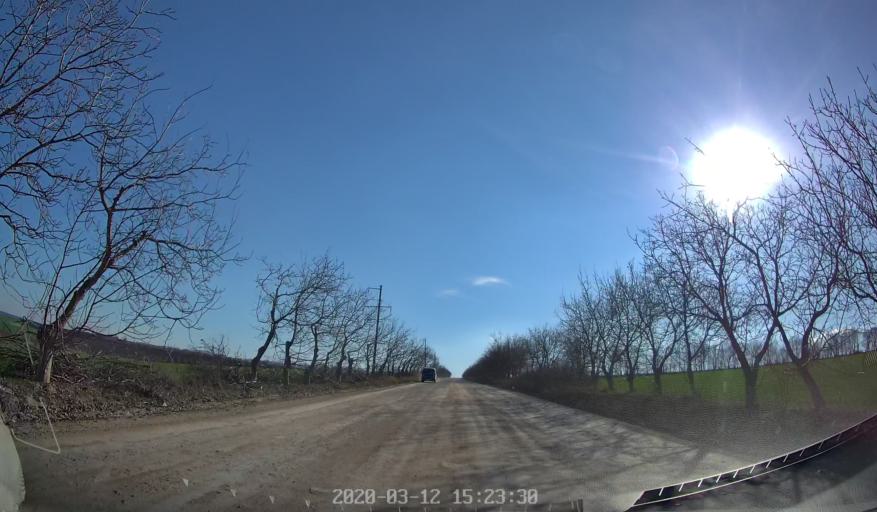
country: MD
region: Chisinau
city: Ciorescu
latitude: 47.1916
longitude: 28.9163
